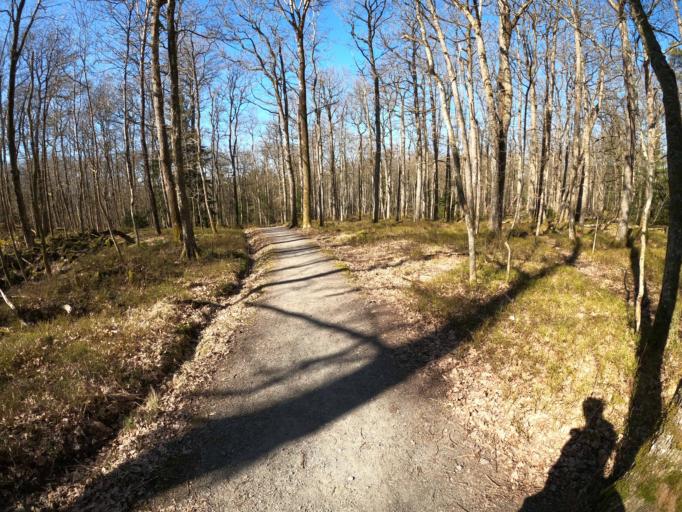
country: SE
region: Vaestra Goetaland
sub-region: Harryda Kommun
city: Molnlycke
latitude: 57.6227
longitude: 12.1120
